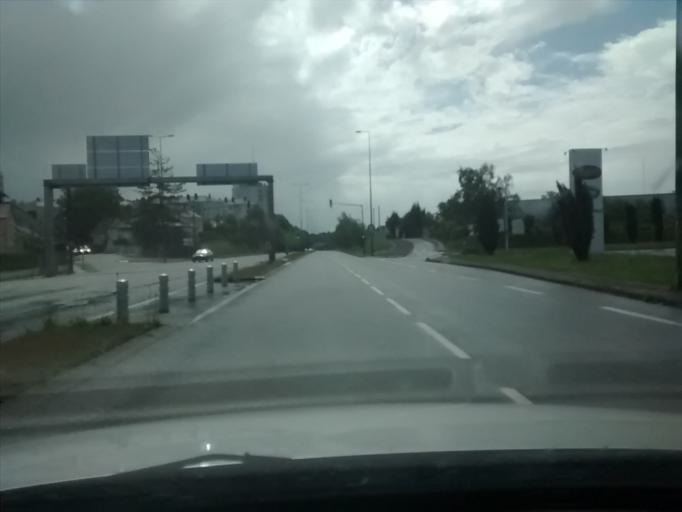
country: FR
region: Pays de la Loire
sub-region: Departement de la Mayenne
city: Laval
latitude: 48.0690
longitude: -0.7916
